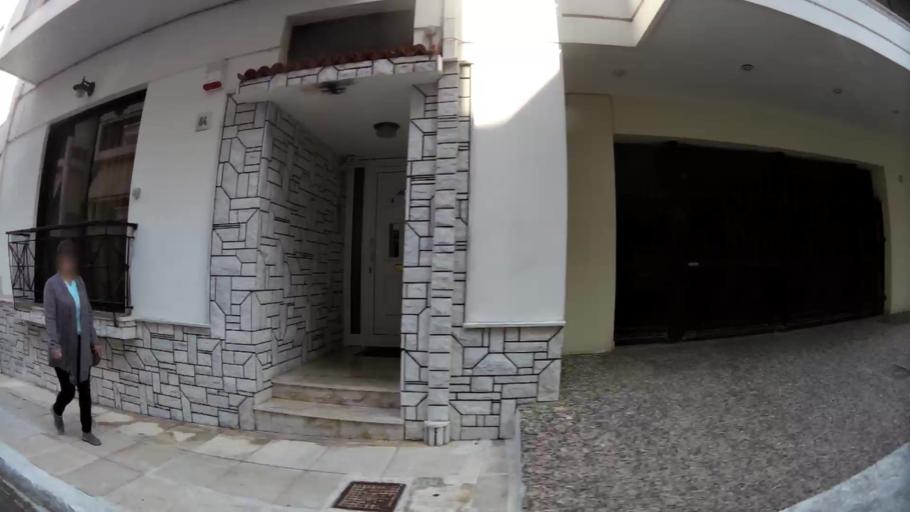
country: GR
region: Attica
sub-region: Nomos Piraios
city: Drapetsona
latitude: 37.9499
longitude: 23.6235
